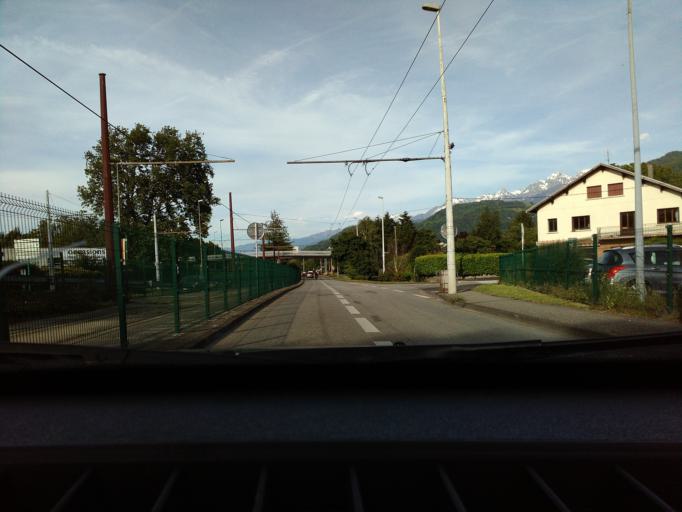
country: FR
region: Rhone-Alpes
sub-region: Departement de l'Isere
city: Eybens
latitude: 45.1602
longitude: 5.7407
